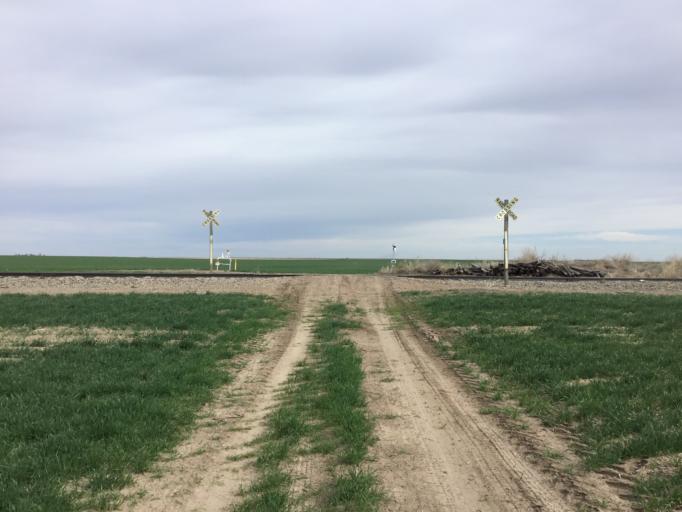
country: US
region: Colorado
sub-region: Kit Carson County
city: Burlington
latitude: 39.3364
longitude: -102.0047
